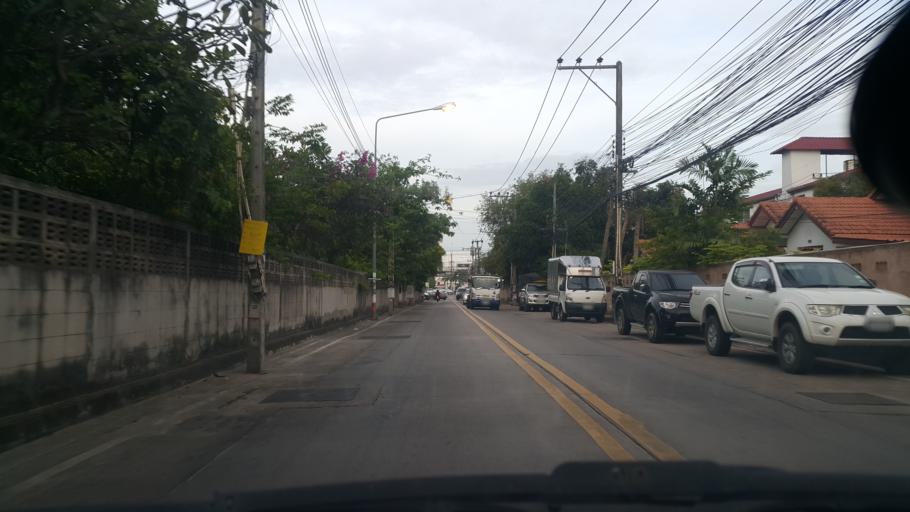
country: TH
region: Chon Buri
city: Phatthaya
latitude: 12.9531
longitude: 100.9045
